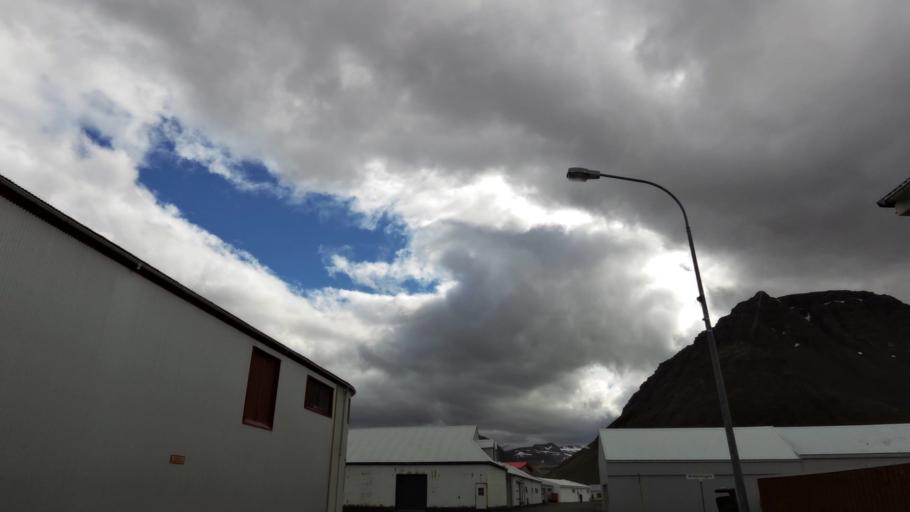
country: IS
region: Westfjords
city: Isafjoerdur
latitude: 66.1592
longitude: -23.2467
